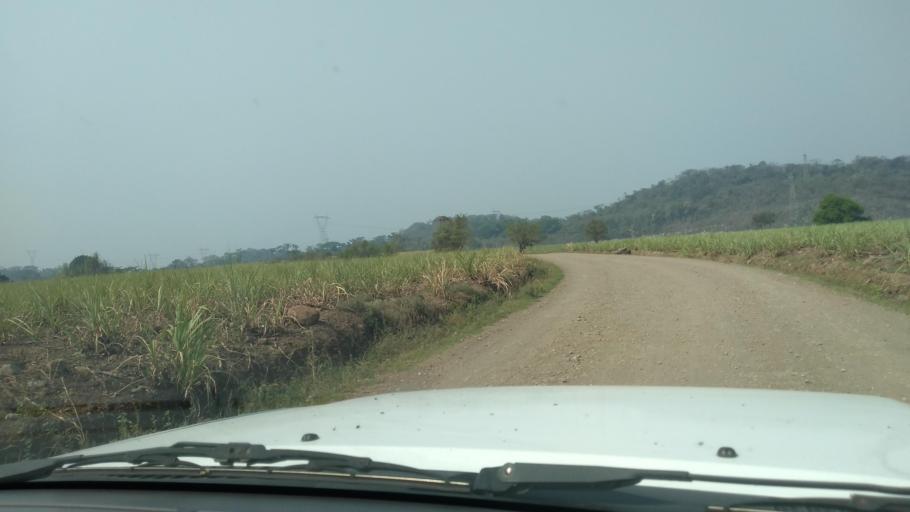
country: MX
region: Oaxaca
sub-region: Cosolapa
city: Cosolapa
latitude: 18.6182
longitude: -96.6307
